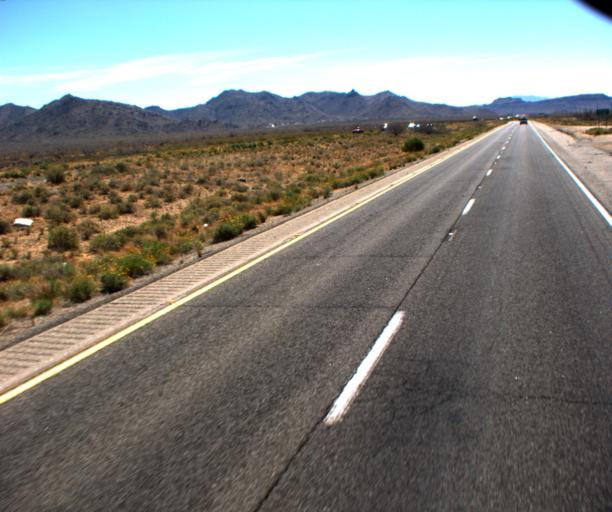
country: US
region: Arizona
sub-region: Mohave County
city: Golden Valley
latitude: 35.2847
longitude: -114.1784
